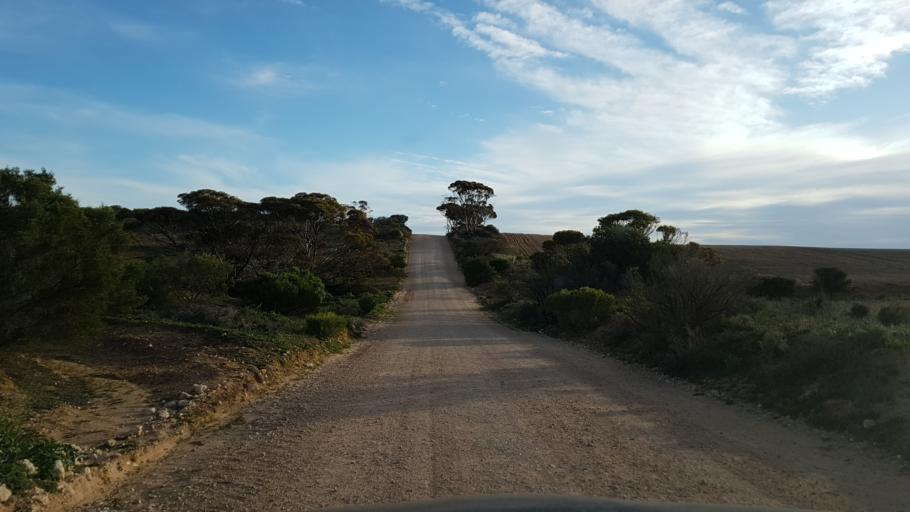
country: AU
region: South Australia
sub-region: Mid Murray
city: Mannum
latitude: -34.7527
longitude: 139.5741
